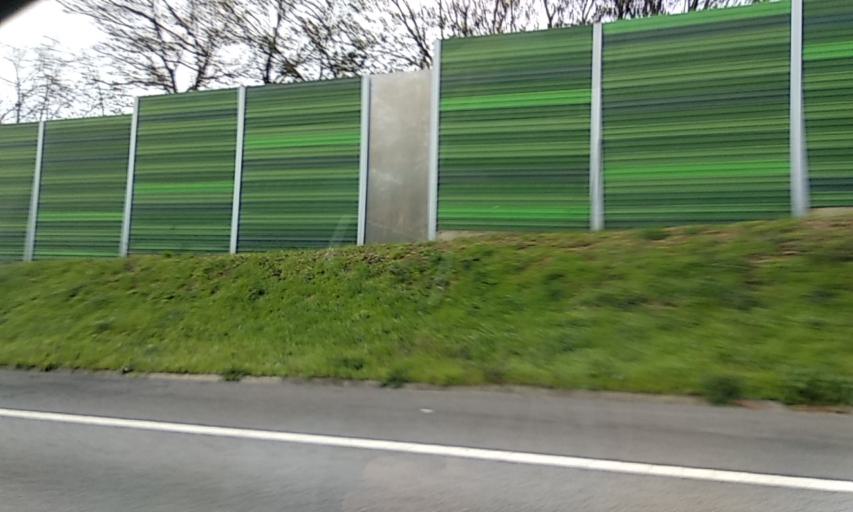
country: PT
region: Porto
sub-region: Santo Tirso
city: Santo Tirso
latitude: 41.3701
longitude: -8.5035
